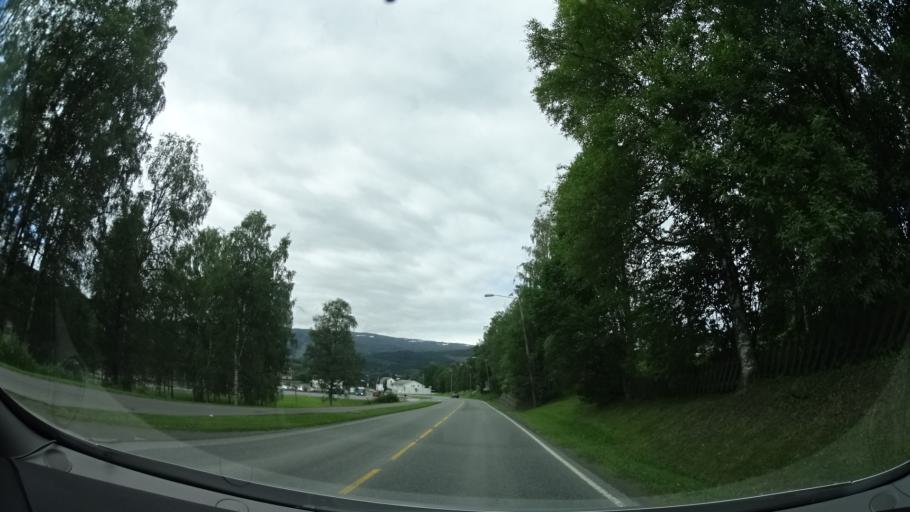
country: NO
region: Nord-Trondelag
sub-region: Meraker
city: Meraker
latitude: 63.4153
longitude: 11.7401
